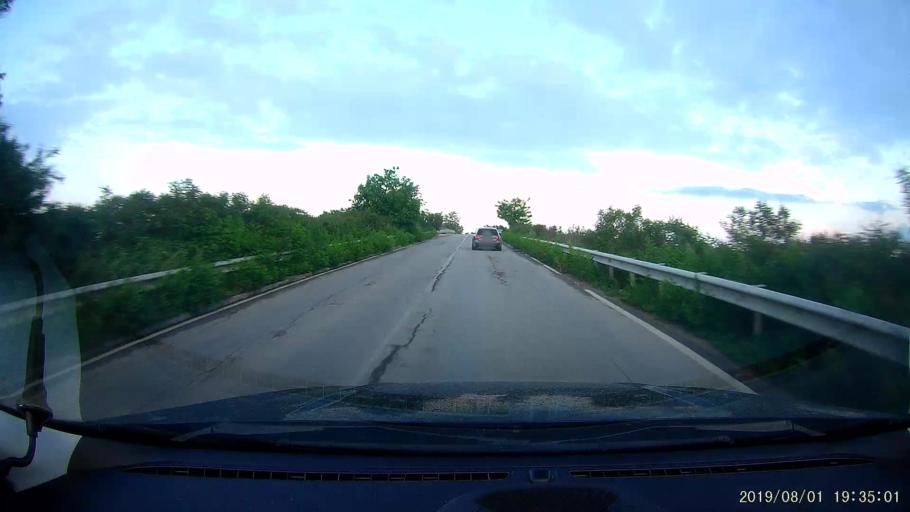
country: BG
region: Burgas
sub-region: Obshtina Sungurlare
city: Sungurlare
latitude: 42.7657
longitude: 26.8801
